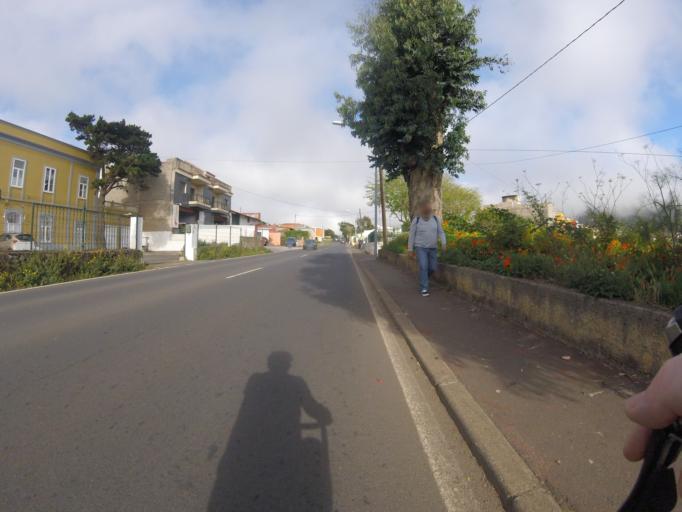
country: ES
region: Canary Islands
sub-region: Provincia de Santa Cruz de Tenerife
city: La Laguna
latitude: 28.4901
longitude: -16.3301
